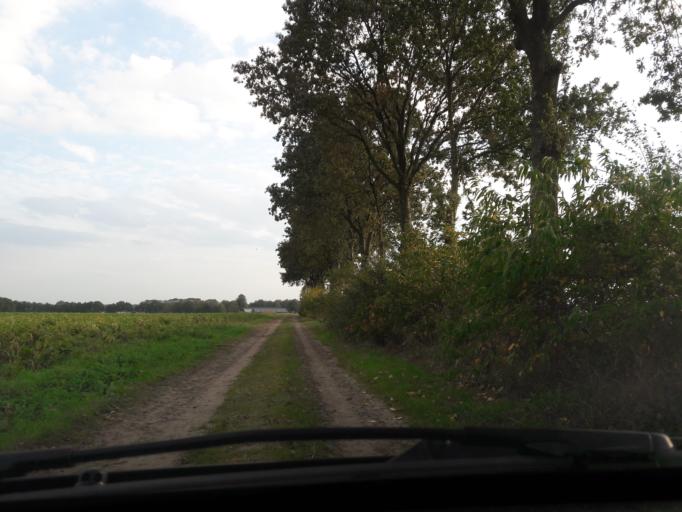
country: NL
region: Drenthe
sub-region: Gemeente Borger-Odoorn
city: Borger
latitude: 52.9532
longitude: 6.8135
